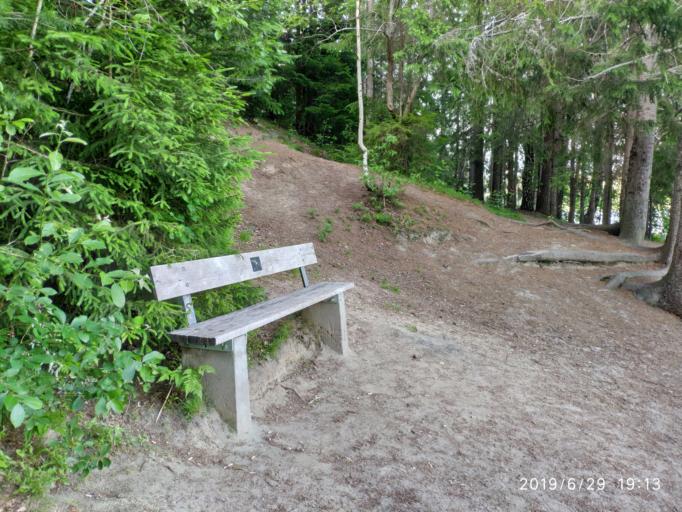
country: NO
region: Akershus
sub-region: Ullensaker
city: Jessheim
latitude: 60.1577
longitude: 11.1622
